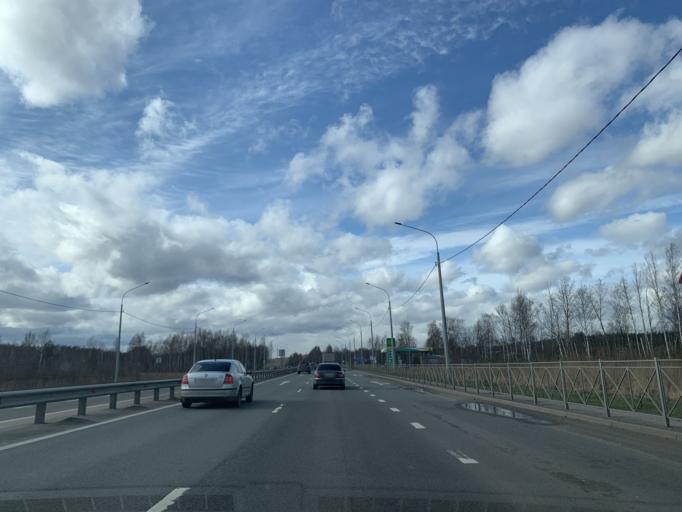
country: RU
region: Jaroslavl
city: Yaroslavl
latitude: 57.6728
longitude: 39.9432
